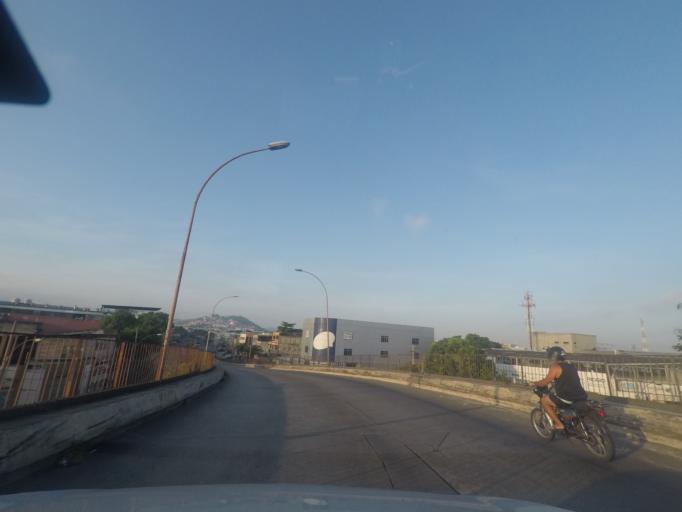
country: BR
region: Rio de Janeiro
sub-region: Duque De Caxias
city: Duque de Caxias
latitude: -22.8269
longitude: -43.2748
